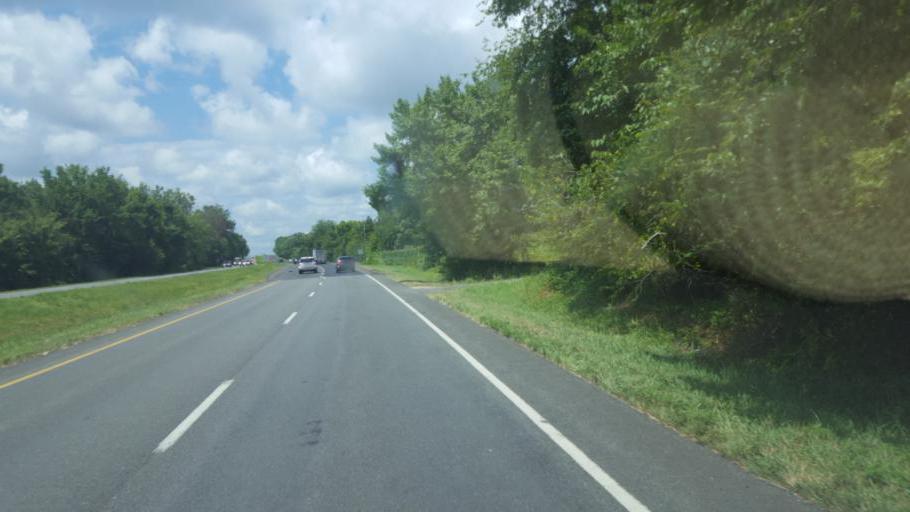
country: US
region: Virginia
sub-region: Fauquier County
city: Bealeton
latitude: 38.6010
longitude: -77.7768
